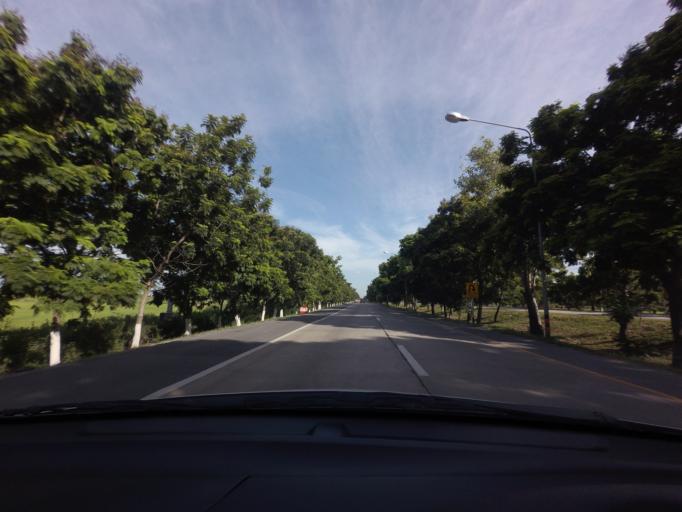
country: TH
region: Suphan Buri
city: Bang Pla Ma
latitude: 14.3781
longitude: 100.1785
